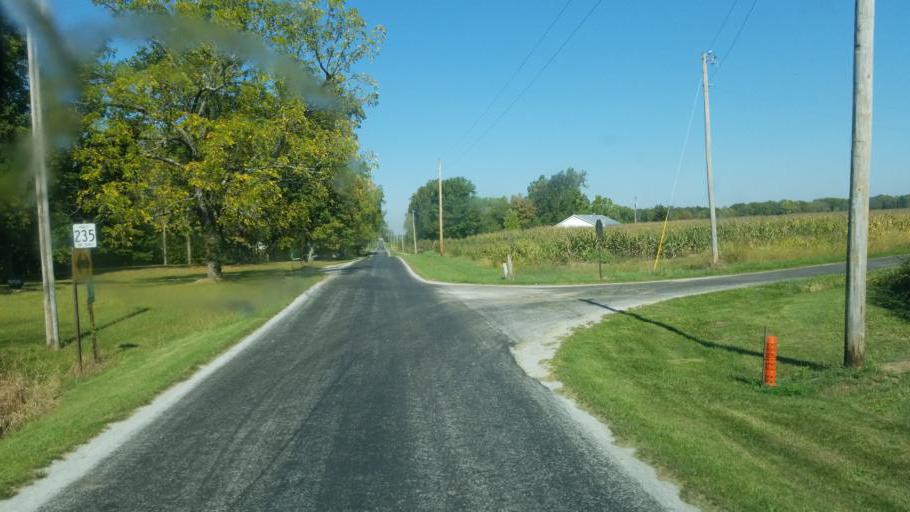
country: US
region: Ohio
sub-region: Hardin County
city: Kenton
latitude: 40.5979
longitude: -83.4817
